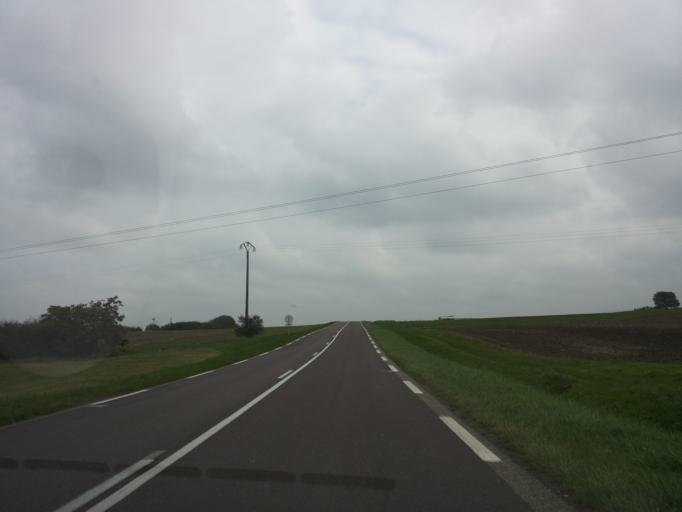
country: FR
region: Lorraine
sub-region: Departement de la Moselle
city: Dieuze
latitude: 48.7192
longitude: 6.7345
